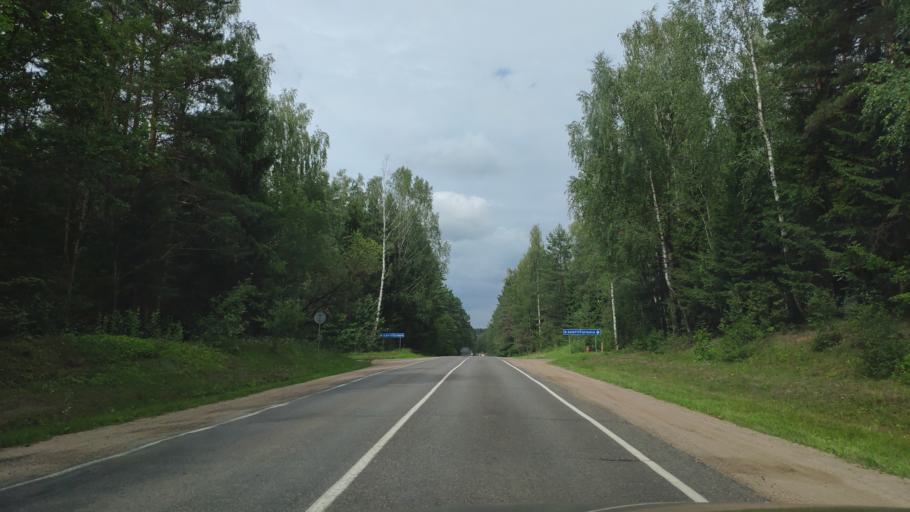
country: BY
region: Minsk
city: Novosel'ye
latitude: 53.9439
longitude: 27.2450
